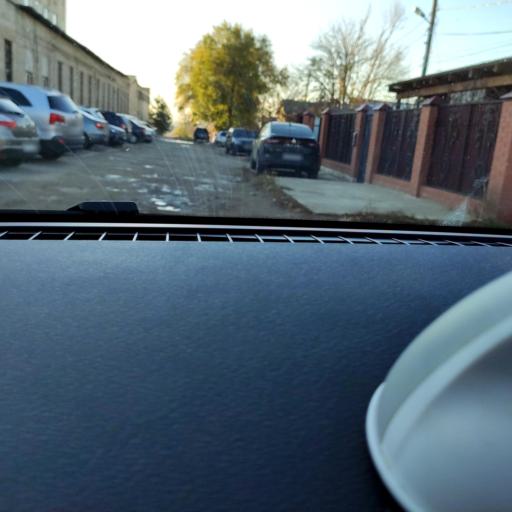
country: RU
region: Samara
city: Samara
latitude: 53.1846
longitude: 50.1979
